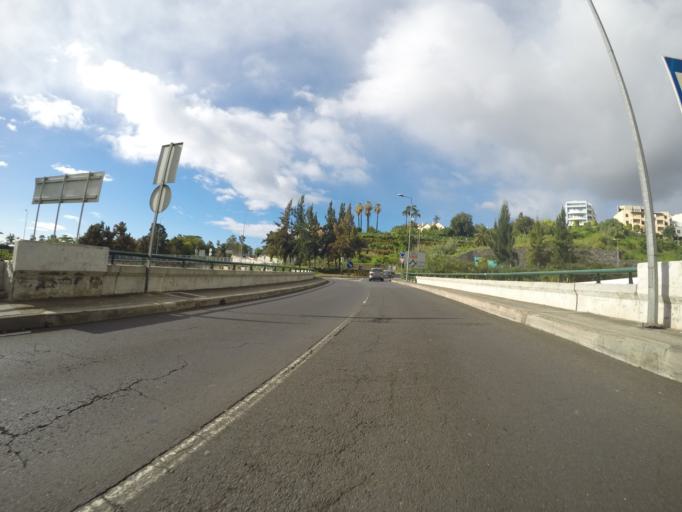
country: PT
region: Madeira
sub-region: Funchal
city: Funchal
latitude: 32.6466
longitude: -16.9235
